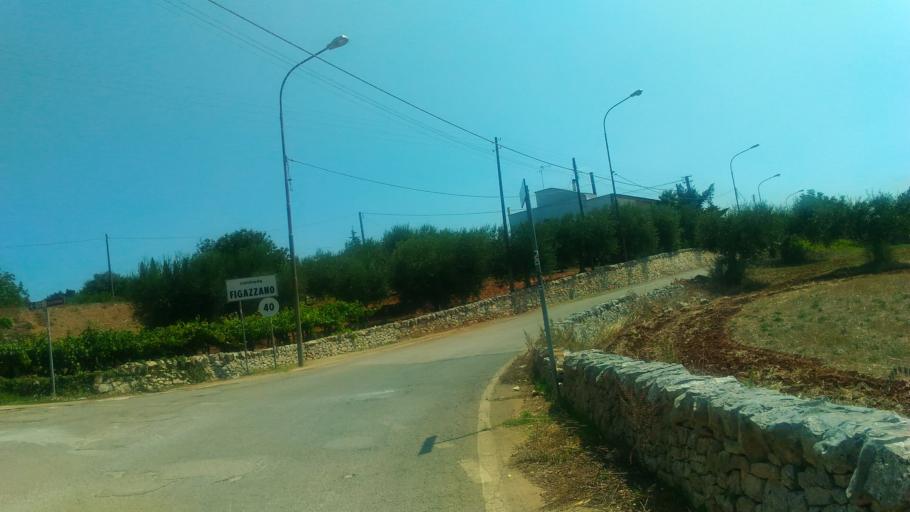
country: IT
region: Apulia
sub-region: Provincia di Bari
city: Locorotondo
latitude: 40.7497
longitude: 17.3705
